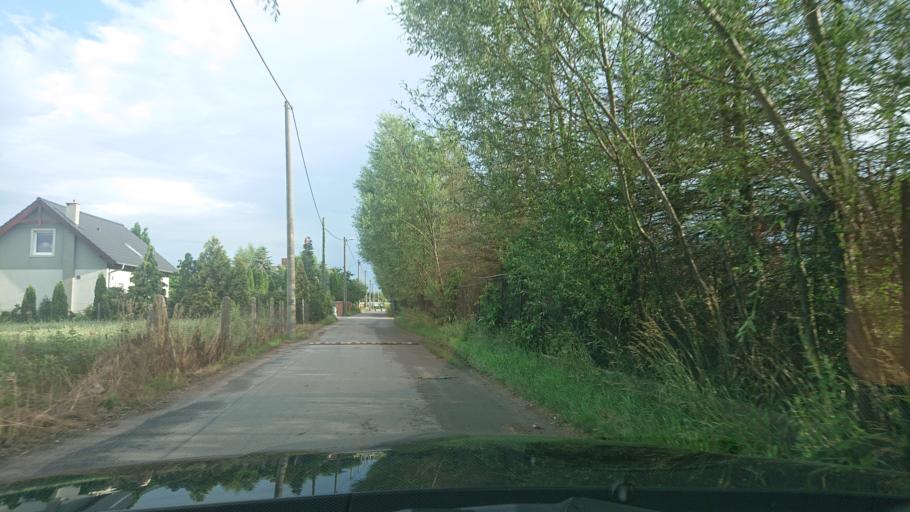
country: PL
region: Greater Poland Voivodeship
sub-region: Powiat gnieznienski
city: Gniezno
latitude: 52.5638
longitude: 17.6145
